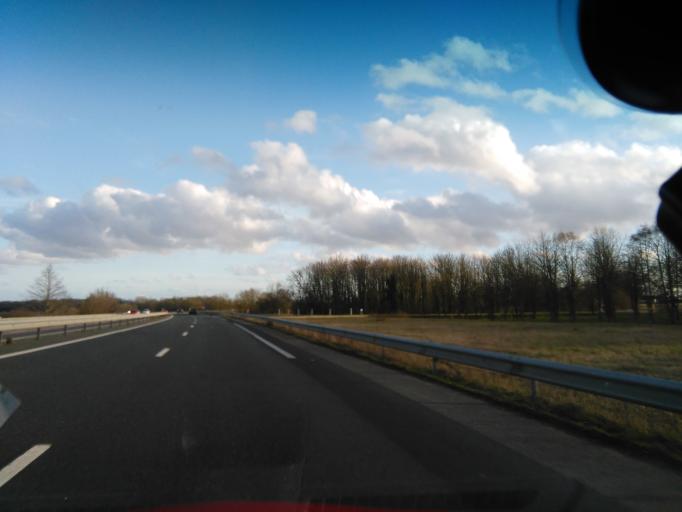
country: FR
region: Lower Normandy
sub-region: Departement du Calvados
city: Potigny
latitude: 48.9814
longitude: -0.2472
